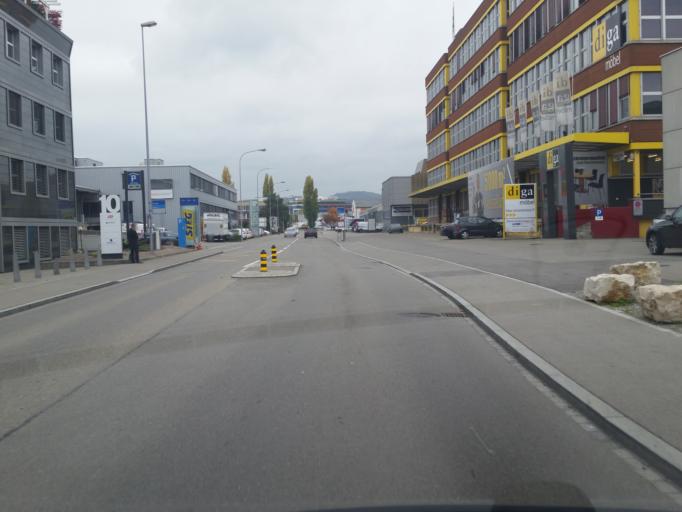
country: CH
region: Zurich
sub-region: Bezirk Dietikon
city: Dietikon / Vorstadt
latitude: 47.4181
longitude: 8.3990
